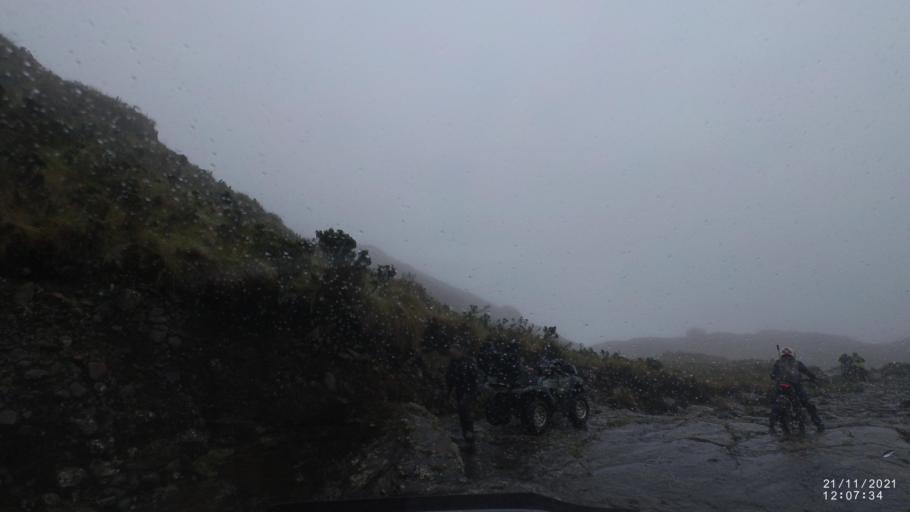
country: BO
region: Cochabamba
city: Cochabamba
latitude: -16.9447
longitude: -66.2579
